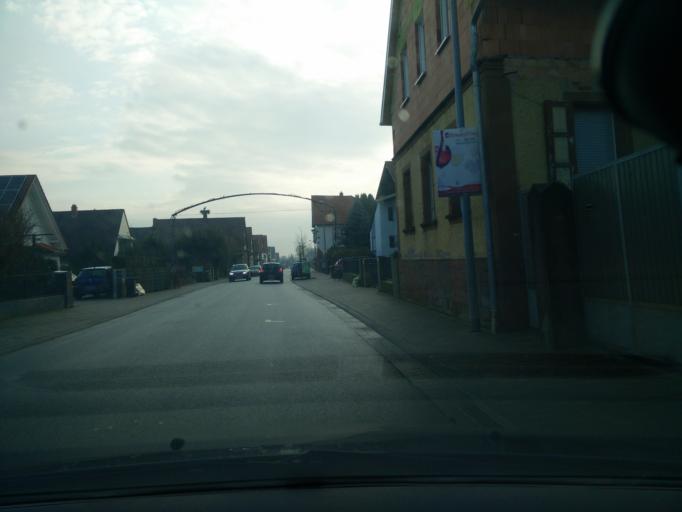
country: DE
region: Rheinland-Pfalz
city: Winden
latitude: 49.0986
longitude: 8.1166
